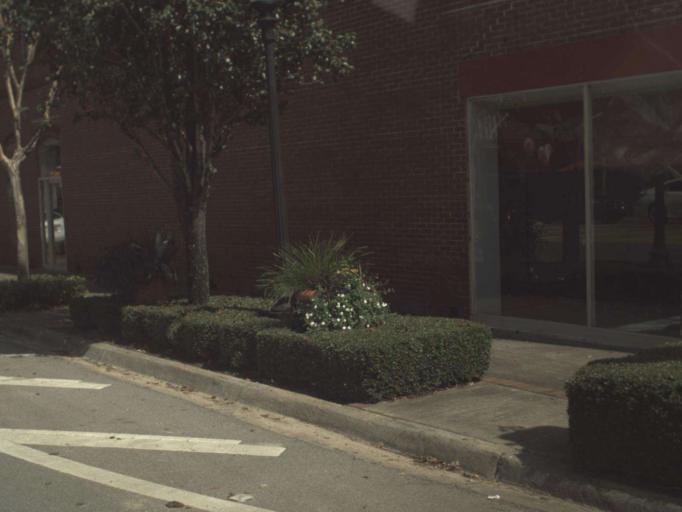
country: US
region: Florida
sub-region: Washington County
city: Chipley
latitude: 30.7808
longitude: -85.5386
